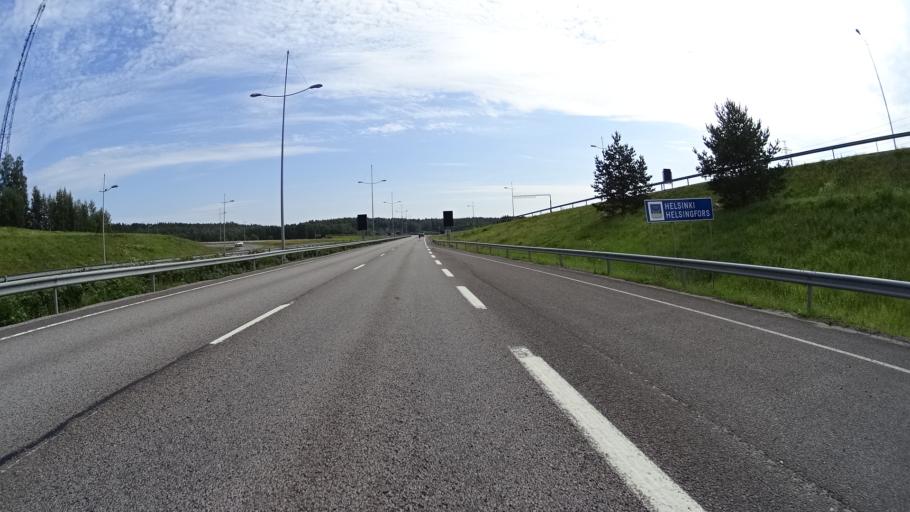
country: FI
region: Uusimaa
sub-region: Helsinki
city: Vantaa
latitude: 60.2448
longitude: 25.1469
